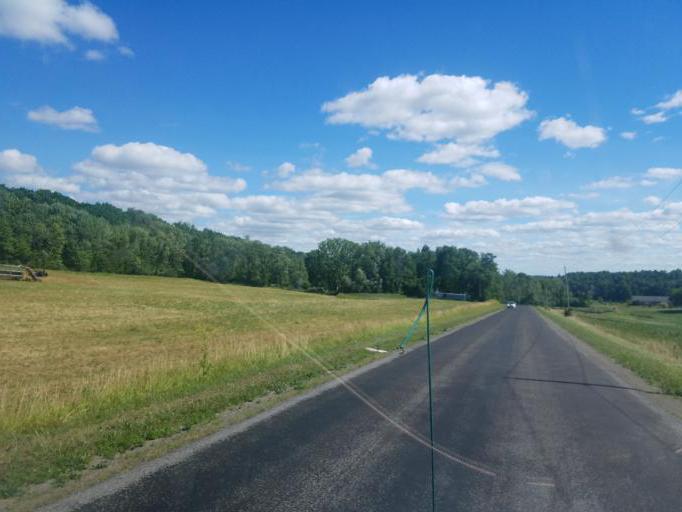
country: US
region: New York
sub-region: Wayne County
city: Lyons
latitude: 43.0962
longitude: -77.0094
